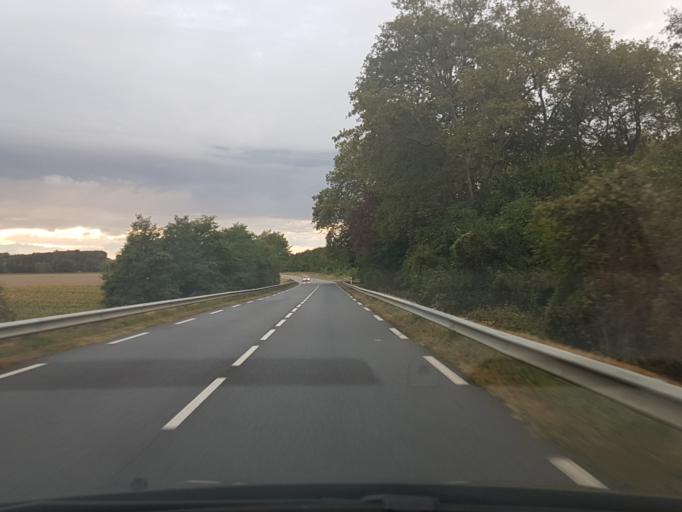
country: FR
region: Midi-Pyrenees
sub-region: Departement de l'Ariege
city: La Tour-du-Crieu
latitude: 43.0835
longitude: 1.7483
